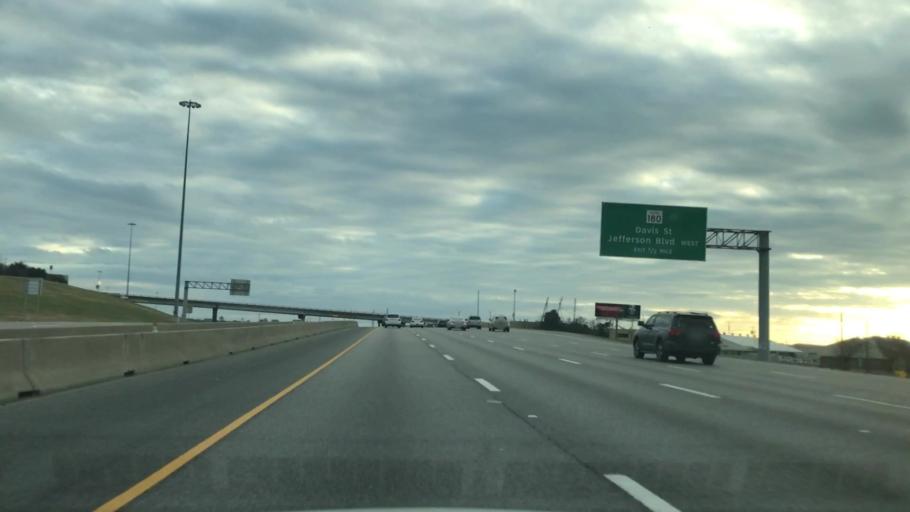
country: US
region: Texas
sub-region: Dallas County
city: Cockrell Hill
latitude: 32.7606
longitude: -96.9169
